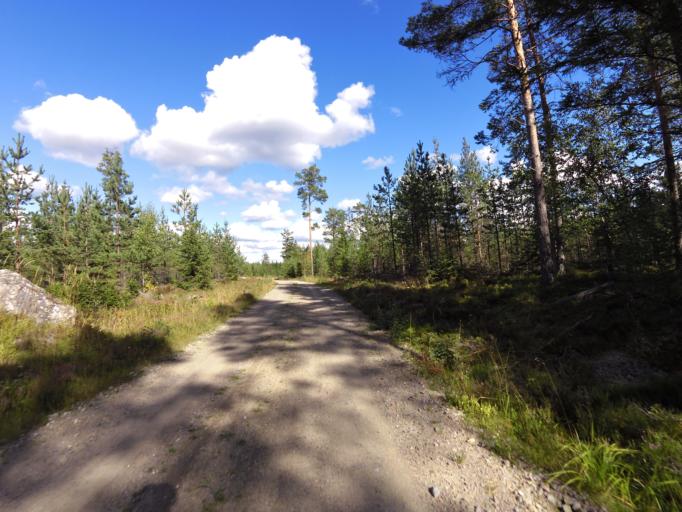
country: SE
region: Gaevleborg
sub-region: Ockelbo Kommun
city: Ockelbo
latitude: 60.8406
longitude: 16.7702
